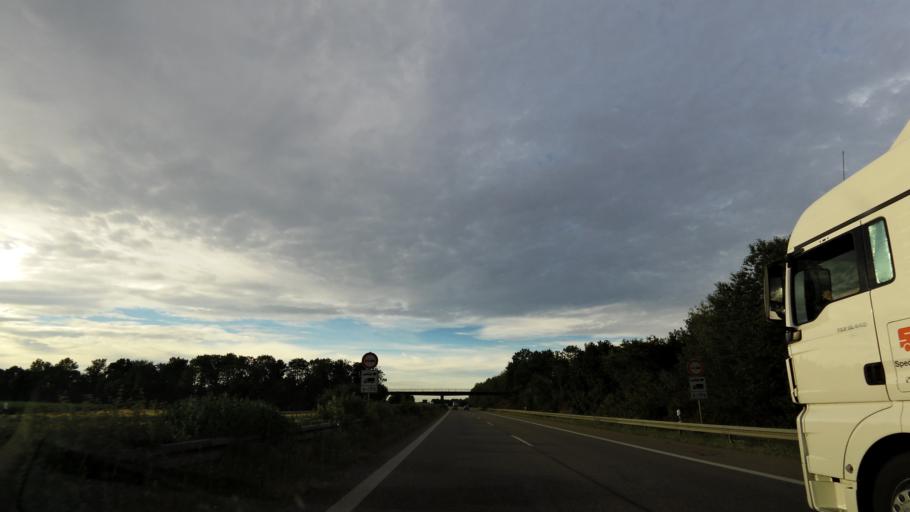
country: DE
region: Baden-Wuerttemberg
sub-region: Freiburg Region
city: Grafenhausen
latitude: 48.2823
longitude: 7.7834
